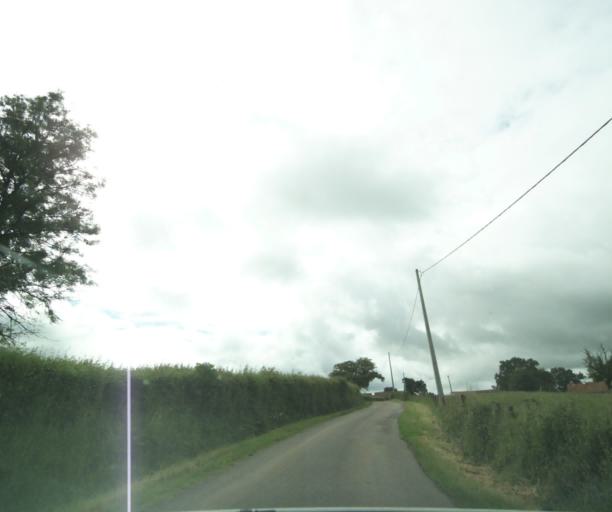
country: FR
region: Bourgogne
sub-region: Departement de Saone-et-Loire
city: Charolles
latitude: 46.4214
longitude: 4.3058
